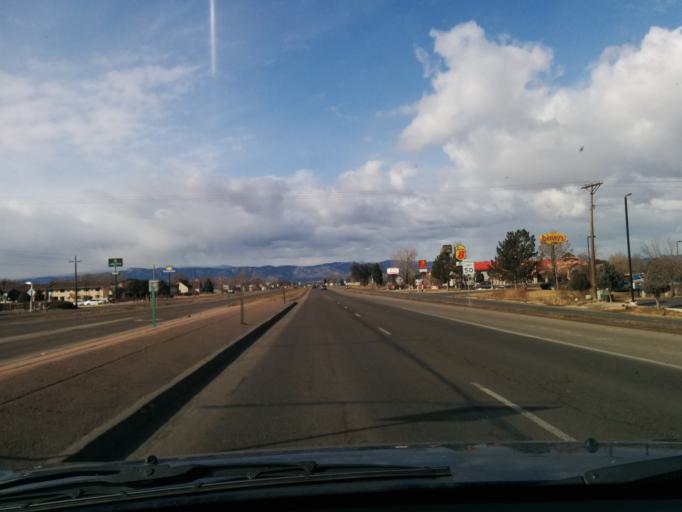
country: US
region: Colorado
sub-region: Larimer County
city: Fort Collins
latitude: 40.5812
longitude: -105.0061
